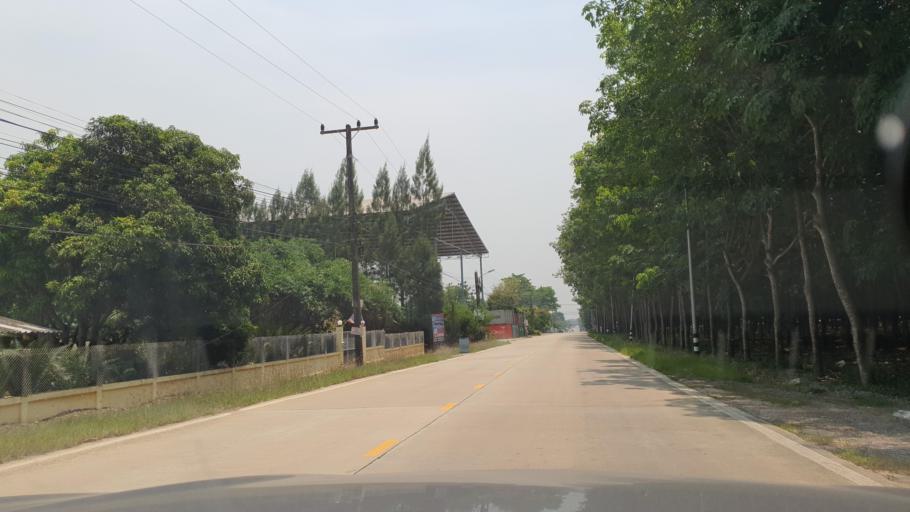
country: TH
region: Rayong
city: Nikhom Phattana
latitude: 12.7894
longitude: 101.1604
